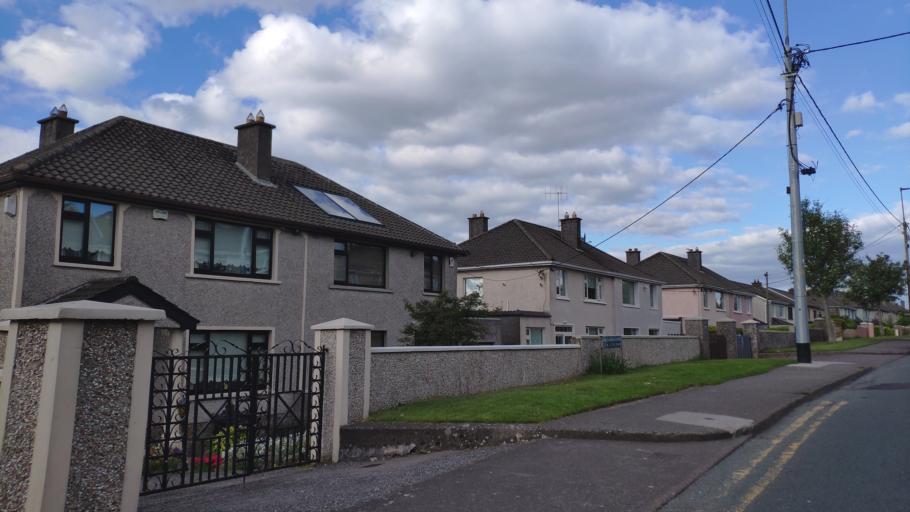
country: IE
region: Munster
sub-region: County Cork
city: Cork
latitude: 51.9104
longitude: -8.4479
